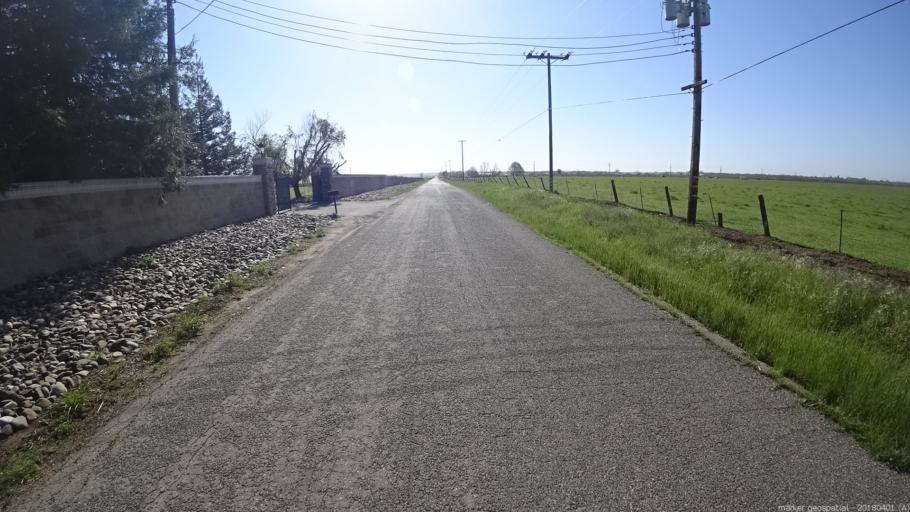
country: US
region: California
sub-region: Sacramento County
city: Rancho Murieta
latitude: 38.4759
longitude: -121.1739
